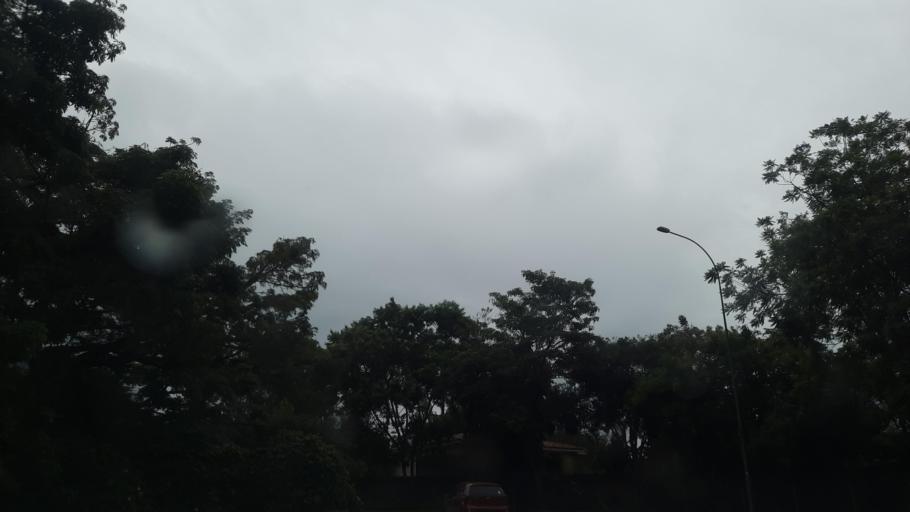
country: SV
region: La Libertad
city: Antiguo Cuscatlan
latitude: 13.6935
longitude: -89.2455
